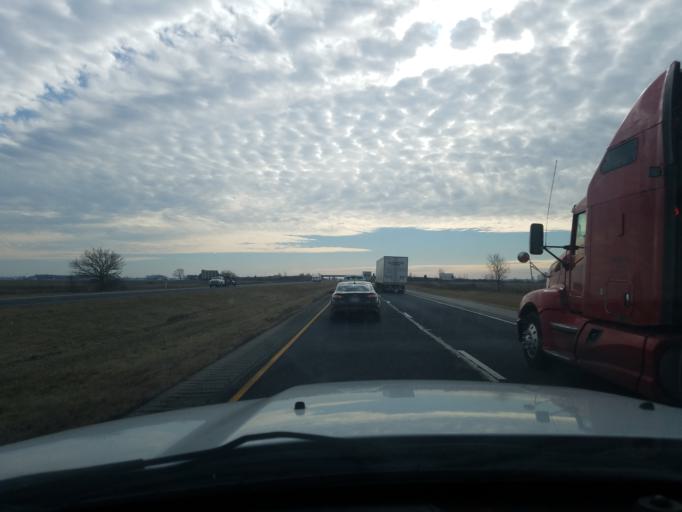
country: US
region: Indiana
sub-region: Huntington County
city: Markle
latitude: 40.8805
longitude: -85.3455
